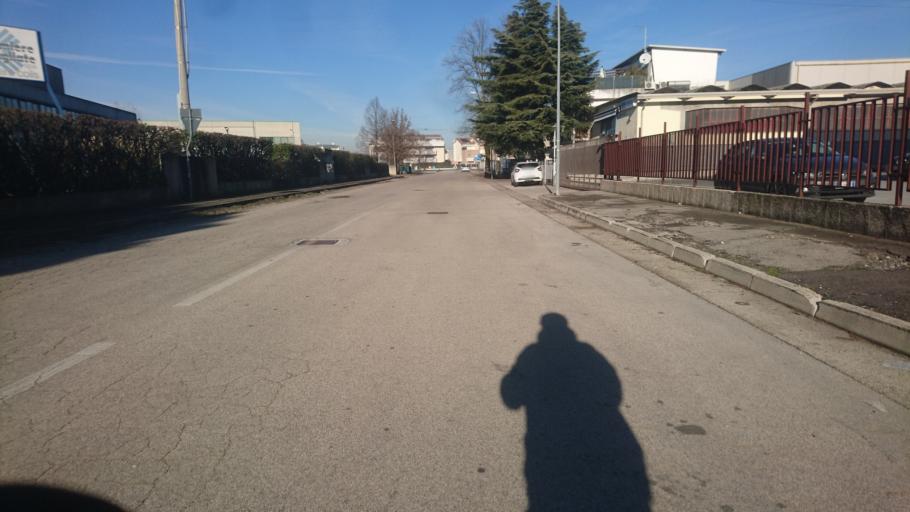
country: IT
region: Veneto
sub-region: Provincia di Padova
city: Limena
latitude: 45.4673
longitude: 11.8431
